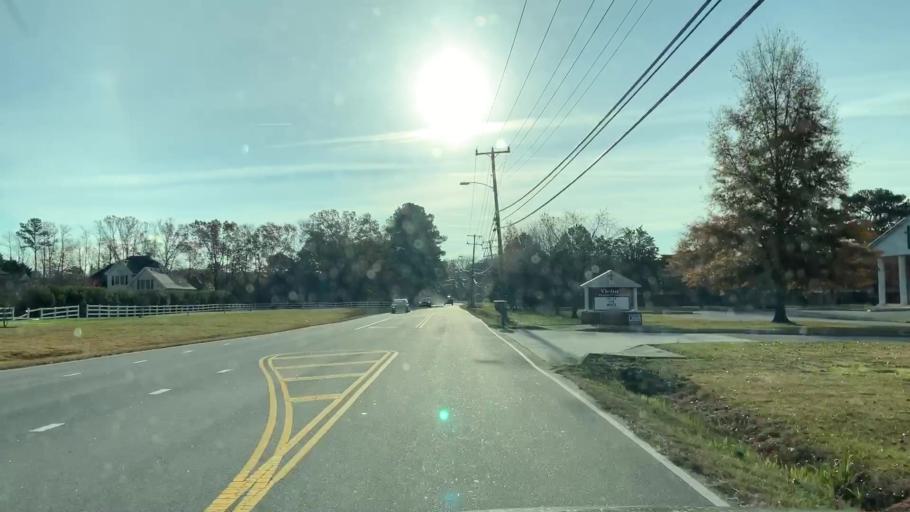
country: US
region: Virginia
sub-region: City of Chesapeake
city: Chesapeake
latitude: 36.7576
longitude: -76.1351
